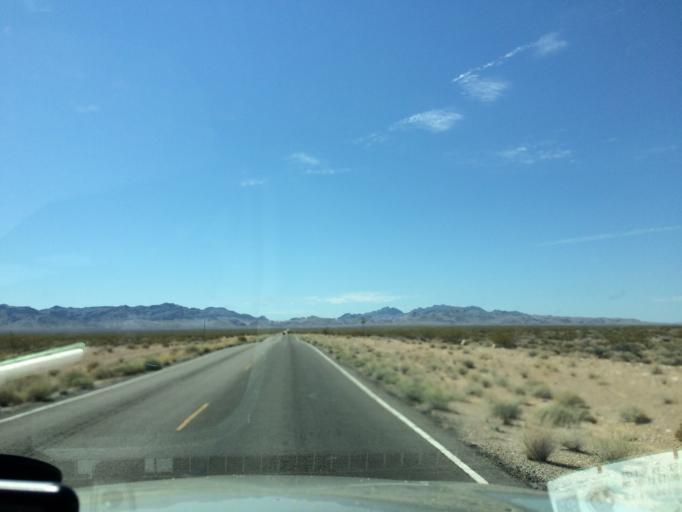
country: US
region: Nevada
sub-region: Clark County
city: Moapa Town
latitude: 36.4742
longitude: -114.7429
